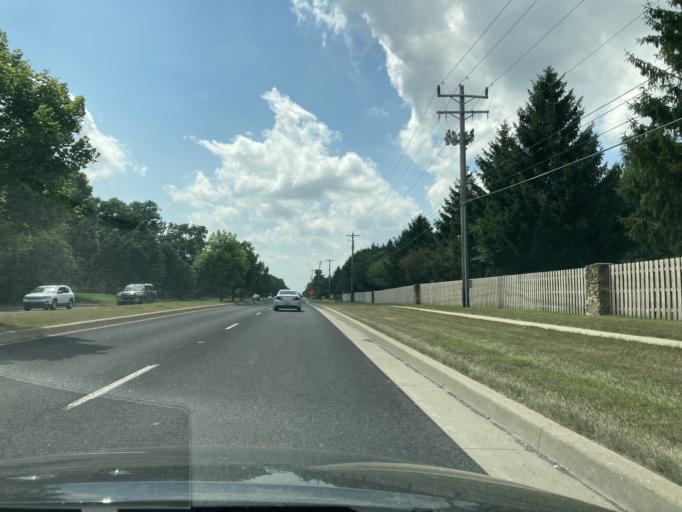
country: US
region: Indiana
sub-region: Hamilton County
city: Carmel
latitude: 39.9998
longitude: -86.1512
